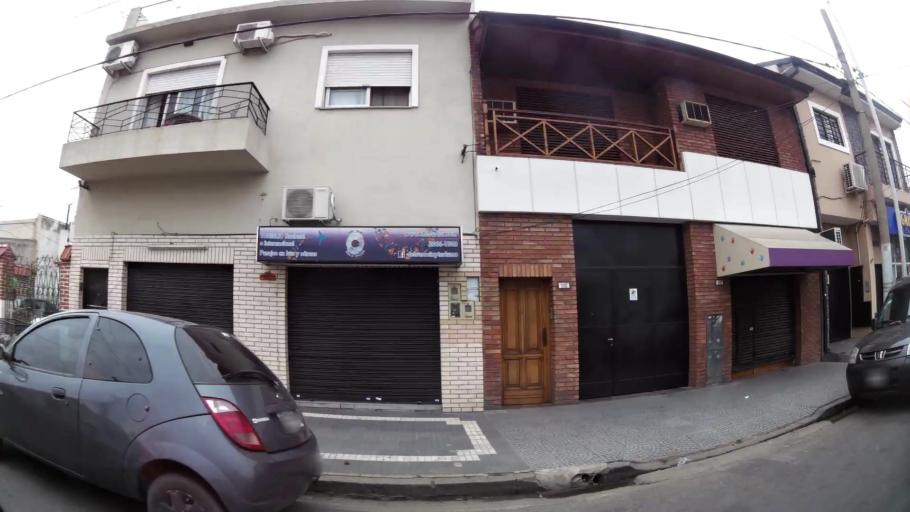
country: AR
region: Buenos Aires
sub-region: Partido de Lanus
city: Lanus
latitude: -34.6866
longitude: -58.3760
